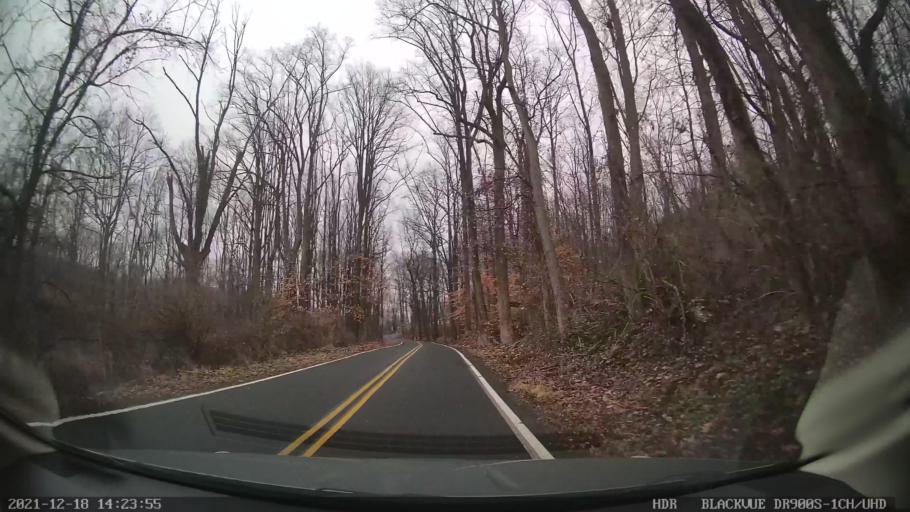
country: US
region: Pennsylvania
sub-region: Berks County
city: Oley
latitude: 40.4245
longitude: -75.7502
